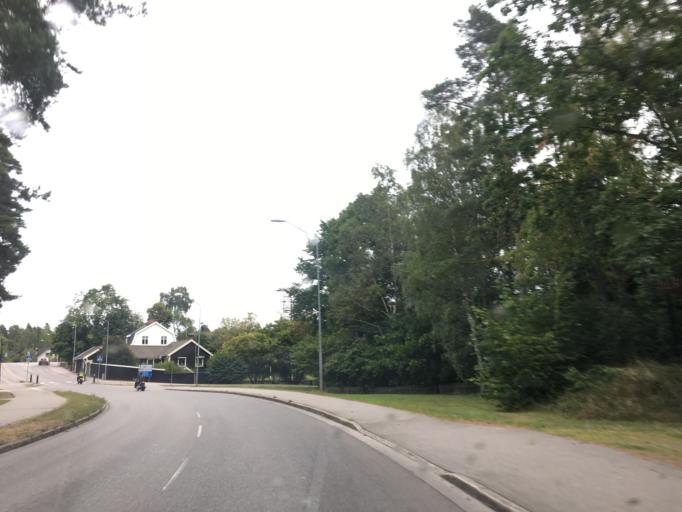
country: SE
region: Kalmar
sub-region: Nybro Kommun
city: Nybro
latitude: 56.7370
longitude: 15.9215
